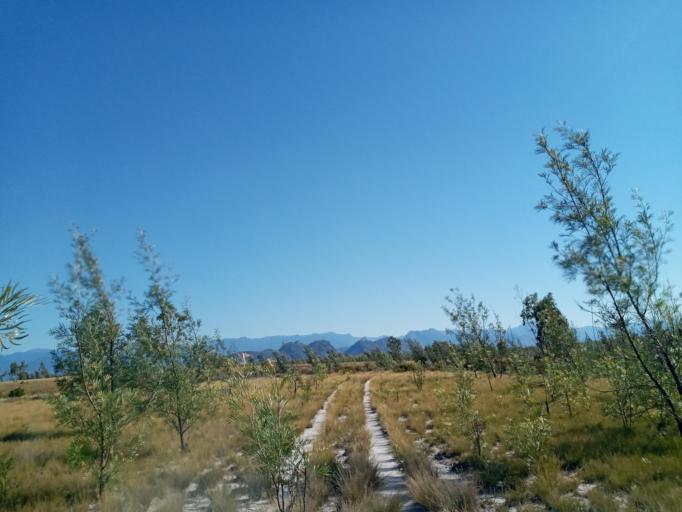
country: MG
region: Atsimo-Atsinanana
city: Vohipaho
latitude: -24.2477
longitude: 47.3170
